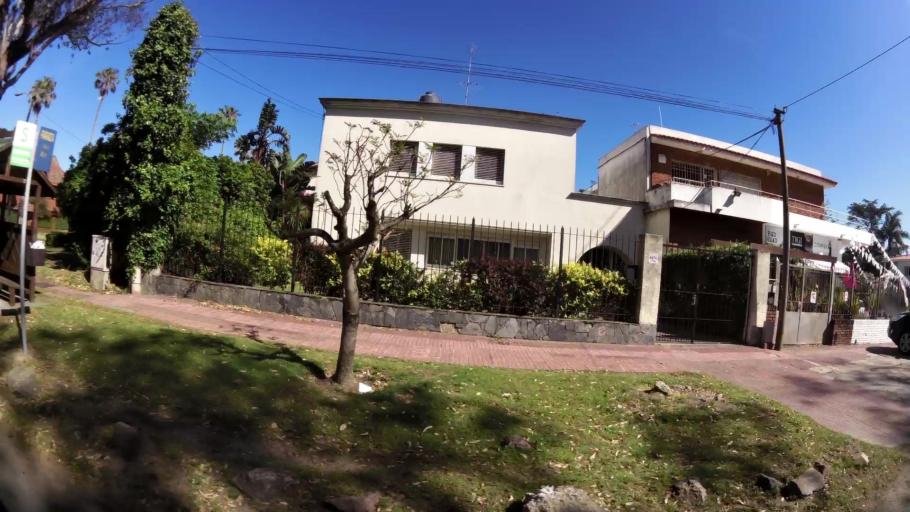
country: UY
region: Canelones
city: Paso de Carrasco
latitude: -34.8845
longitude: -56.0532
